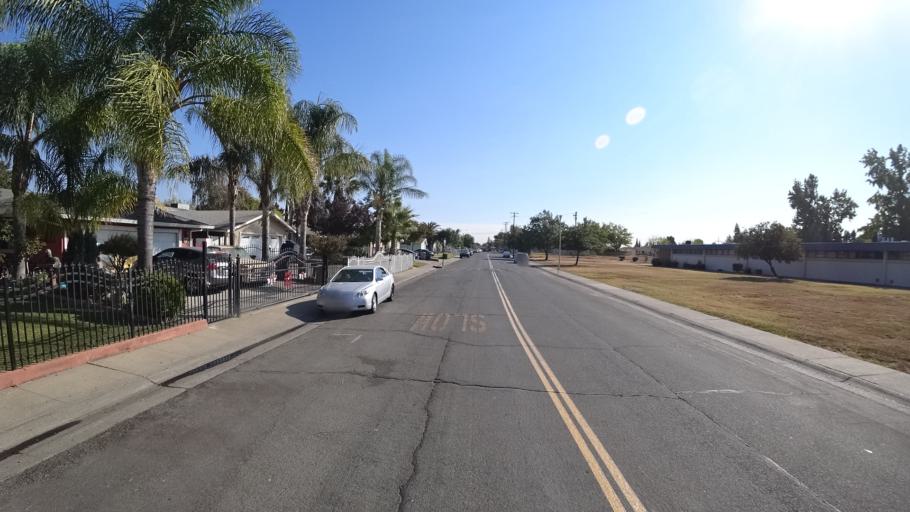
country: US
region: California
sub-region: Sacramento County
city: Parkway
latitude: 38.4774
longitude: -121.4837
